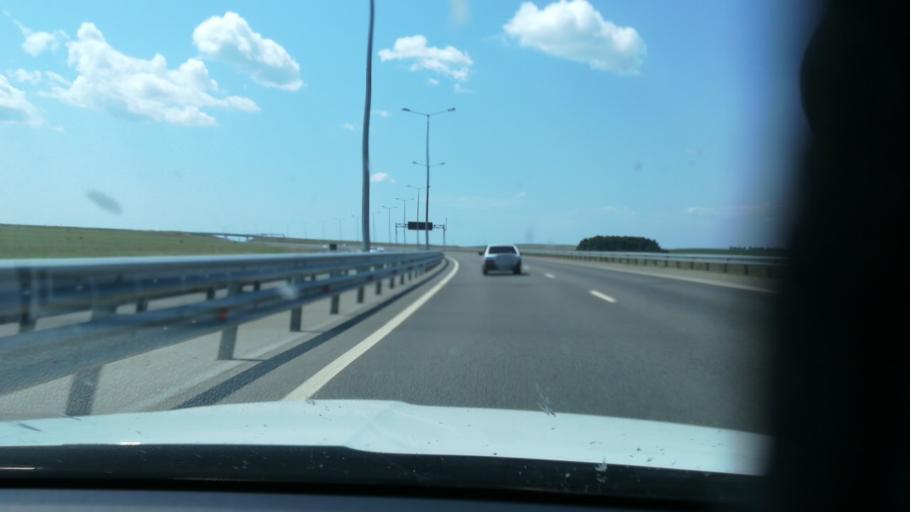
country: RU
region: Krasnodarskiy
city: Vyshestebliyevskaya
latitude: 45.2429
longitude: 37.0560
